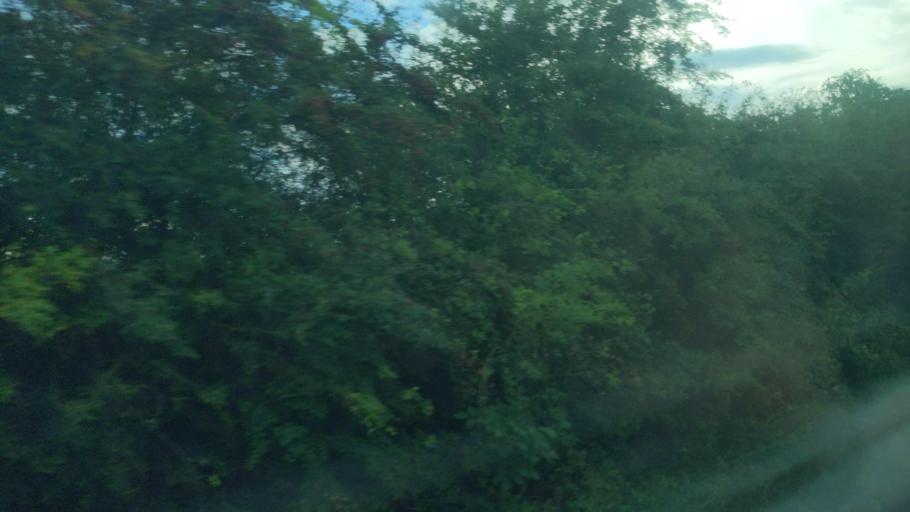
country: CZ
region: Central Bohemia
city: Uvaly
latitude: 50.0773
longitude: 14.7768
